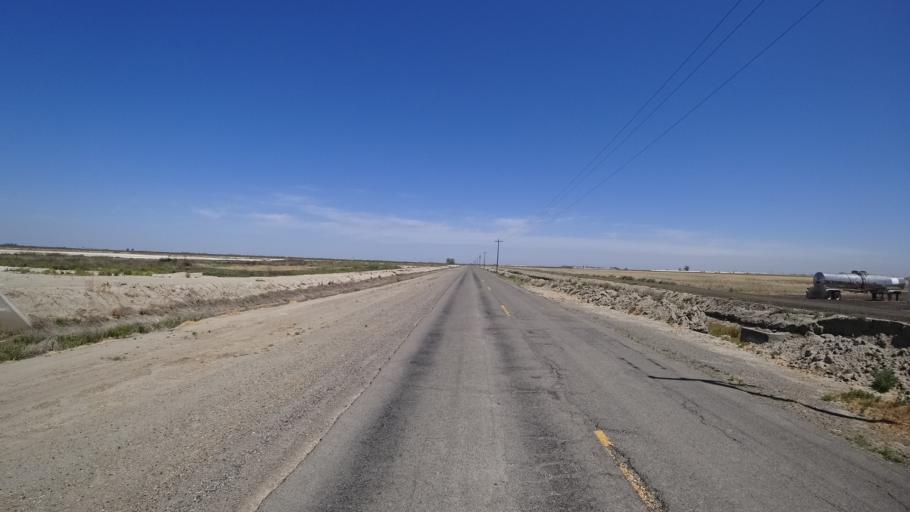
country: US
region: California
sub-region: Kings County
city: Stratford
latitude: 36.1819
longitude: -119.7175
